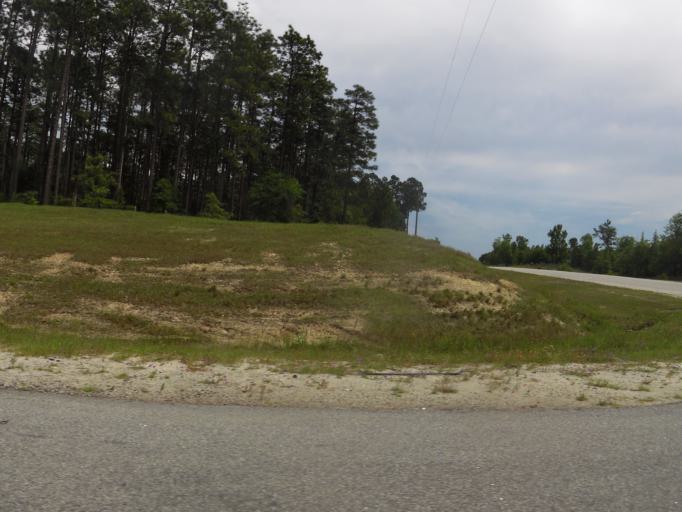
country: US
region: Georgia
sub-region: Emanuel County
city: Swainsboro
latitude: 32.6211
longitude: -82.3770
